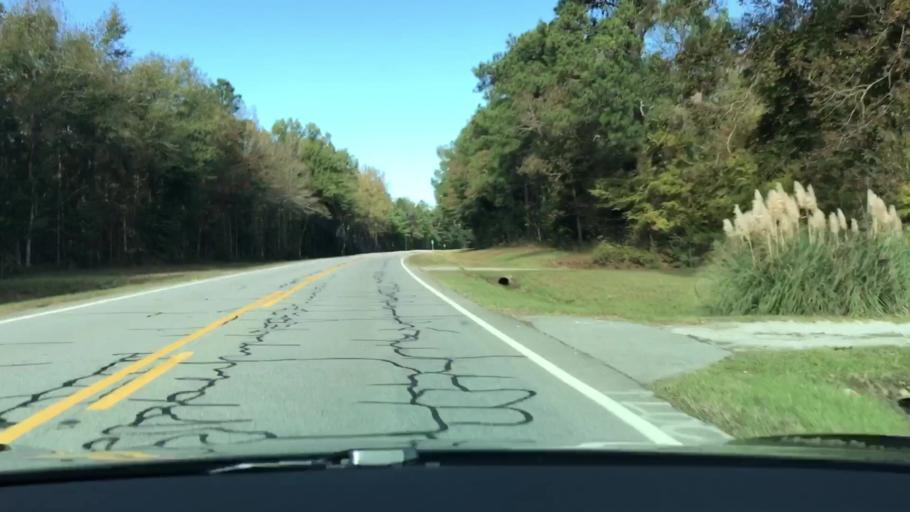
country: US
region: Georgia
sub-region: Warren County
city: Warrenton
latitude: 33.3470
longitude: -82.5822
